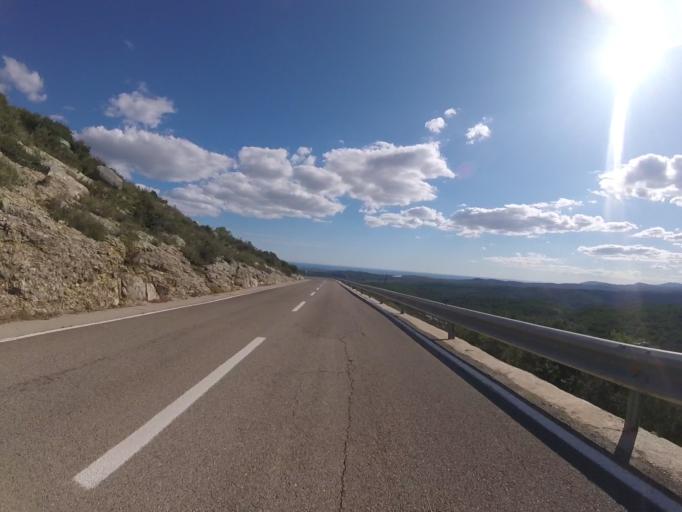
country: ES
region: Valencia
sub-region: Provincia de Castello
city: Alcala de Xivert
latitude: 40.2930
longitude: 0.1813
